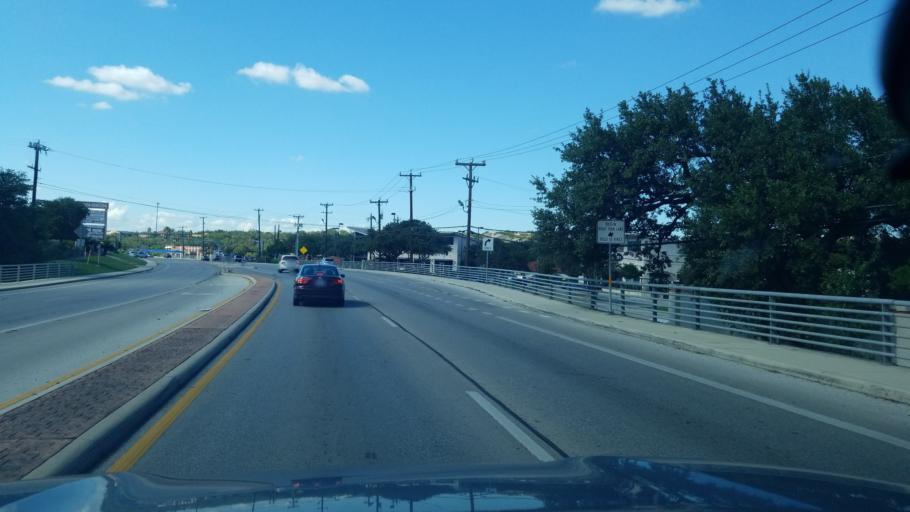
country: US
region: Texas
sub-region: Bexar County
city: Hollywood Park
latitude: 29.6196
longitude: -98.5116
